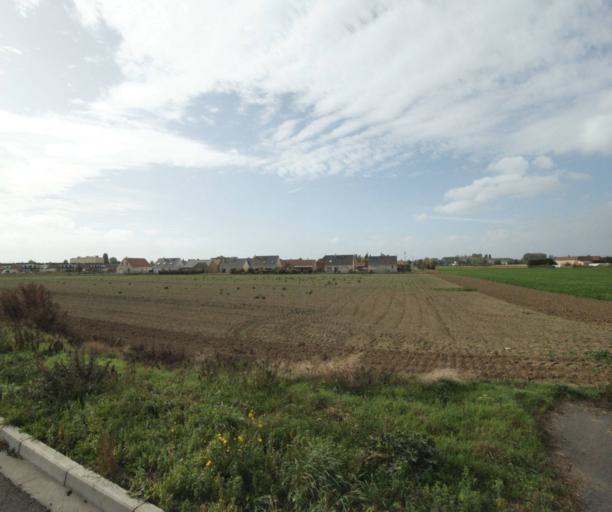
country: FR
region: Nord-Pas-de-Calais
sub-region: Departement du Nord
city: La Bassee
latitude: 50.5419
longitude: 2.8132
